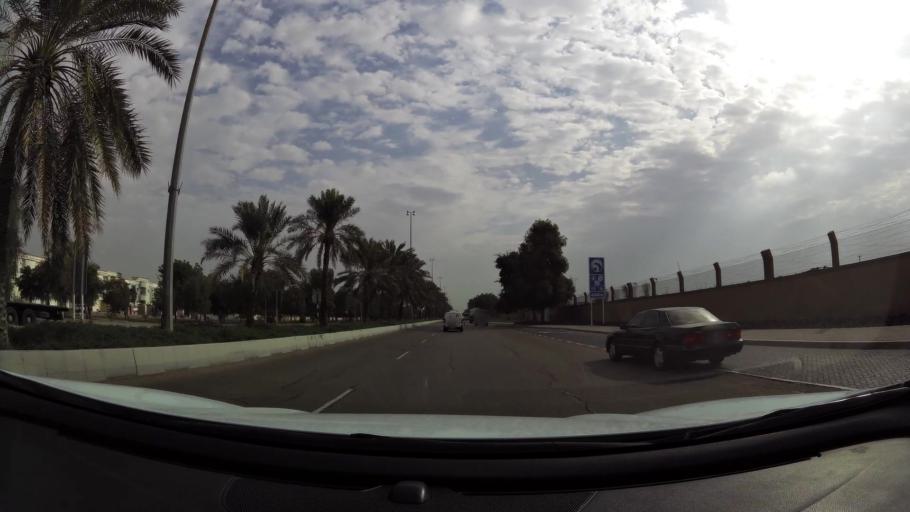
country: AE
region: Abu Dhabi
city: Al Ain
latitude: 24.2082
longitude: 55.6881
